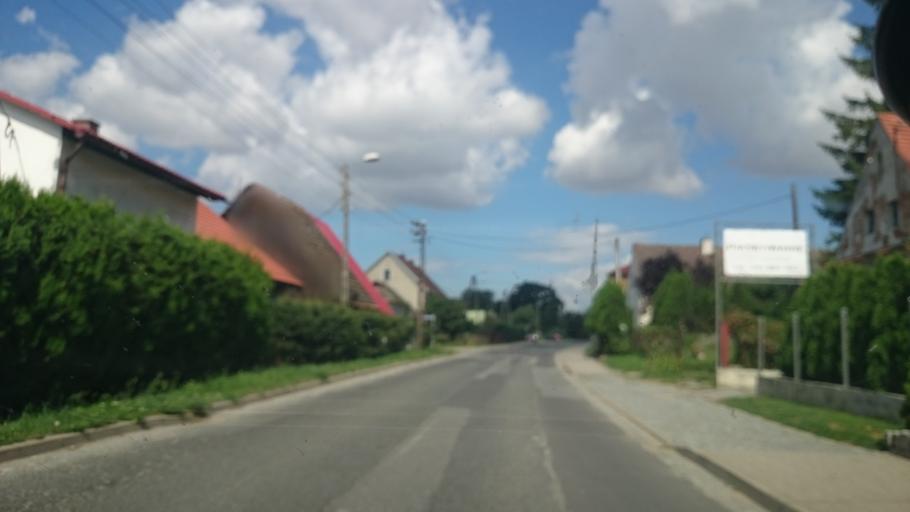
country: PL
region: Lower Silesian Voivodeship
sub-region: Powiat zabkowicki
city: Zabkowice Slaskie
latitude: 50.5823
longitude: 16.8221
